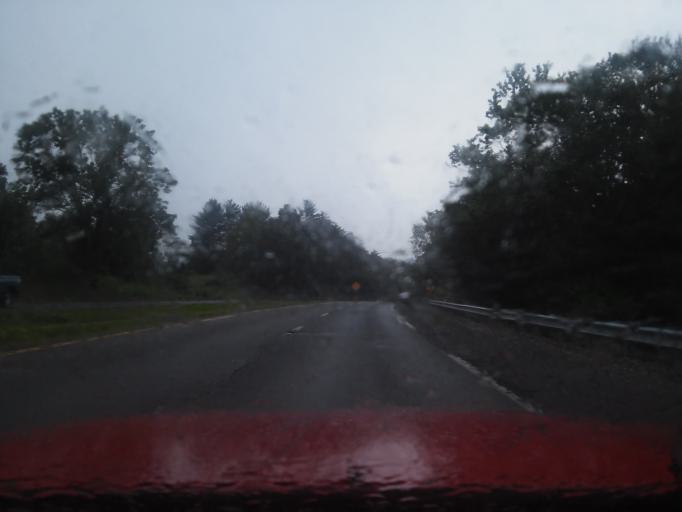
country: US
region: Virginia
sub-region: Montgomery County
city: Prices Fork
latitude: 37.2977
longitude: -80.5026
